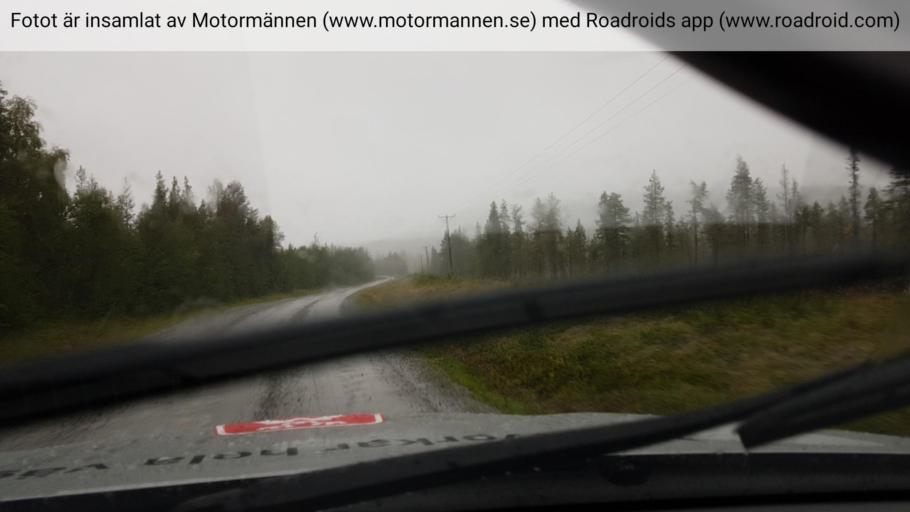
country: SE
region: Norrbotten
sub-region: Jokkmokks Kommun
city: Jokkmokk
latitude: 66.6429
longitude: 18.8718
